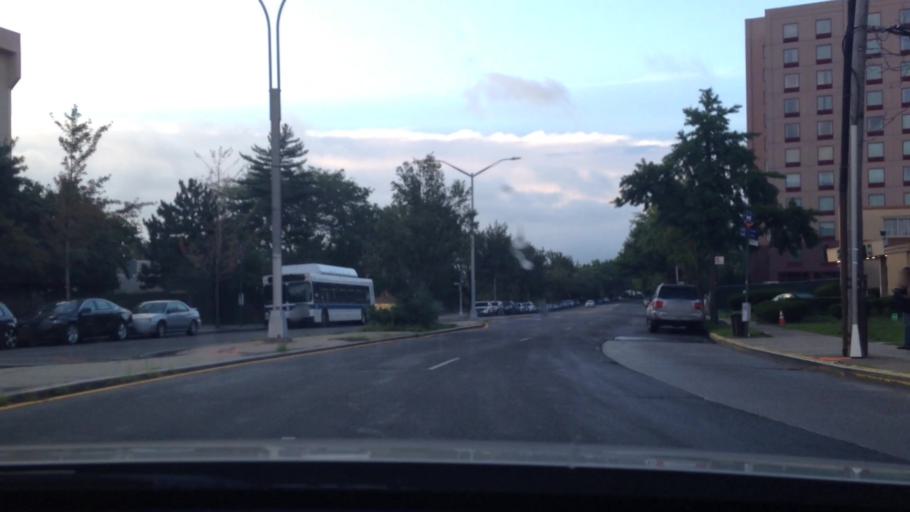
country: US
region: New York
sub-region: Bronx
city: The Bronx
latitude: 40.7689
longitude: -73.8685
